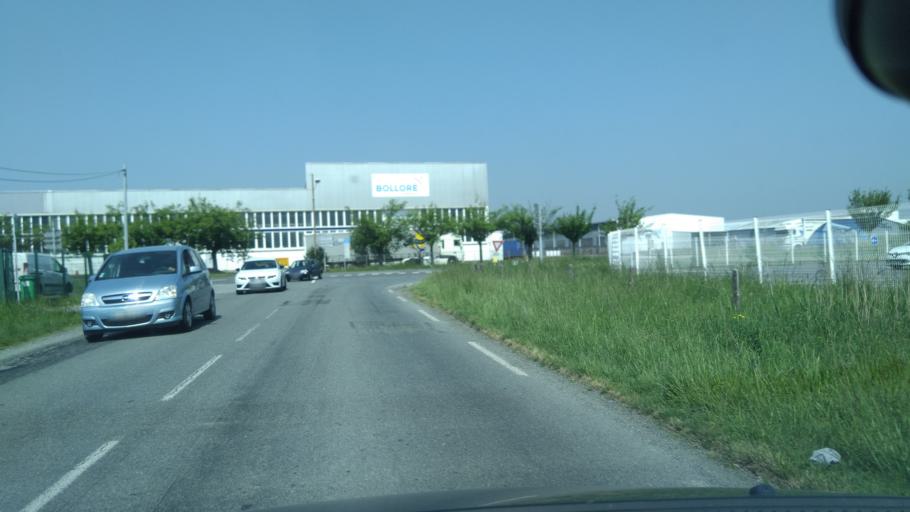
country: FR
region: Pays de la Loire
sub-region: Departement de la Loire-Atlantique
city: Trignac
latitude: 47.3104
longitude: -2.1743
